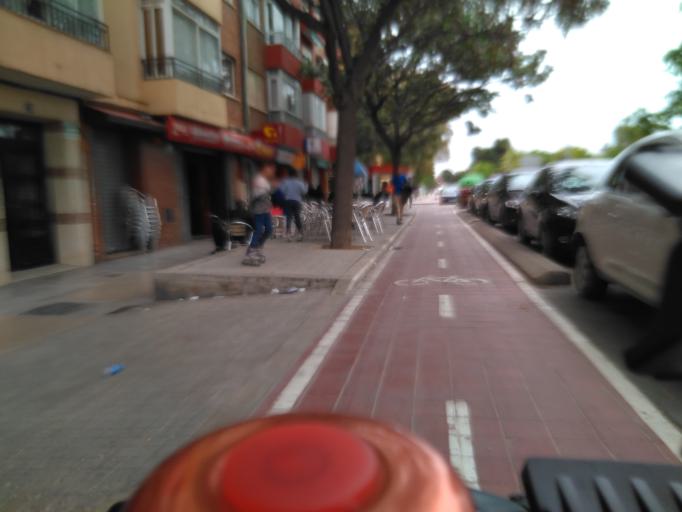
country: ES
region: Valencia
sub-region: Provincia de Valencia
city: Mislata
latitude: 39.4671
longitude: -0.4054
